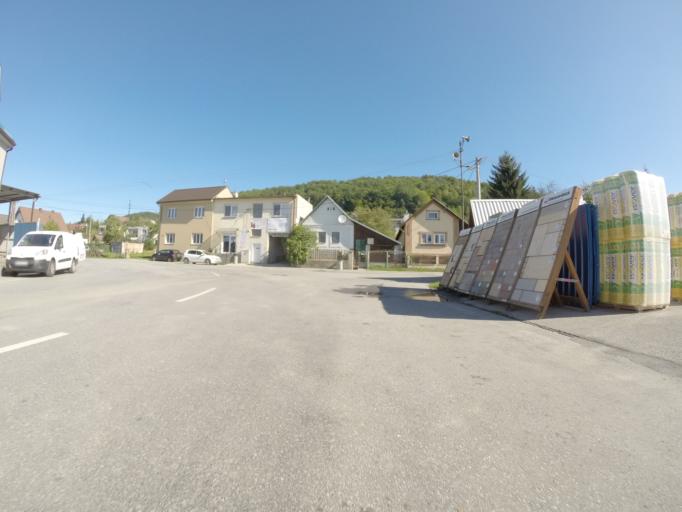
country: SK
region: Trenciansky
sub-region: Okres Povazska Bystrica
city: Povazska Bystrica
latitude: 49.1278
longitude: 18.4296
